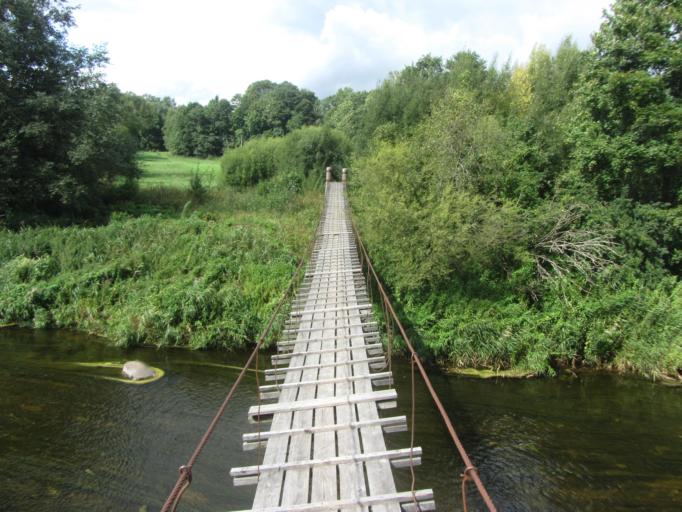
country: LT
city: Silale
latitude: 55.4533
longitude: 22.0270
